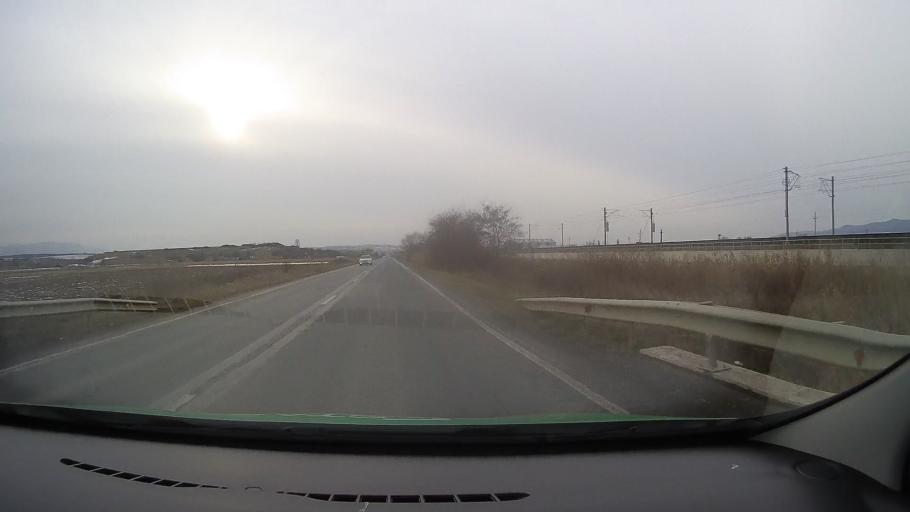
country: RO
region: Hunedoara
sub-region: Municipiul Orastie
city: Orastie
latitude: 45.8728
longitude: 23.2331
